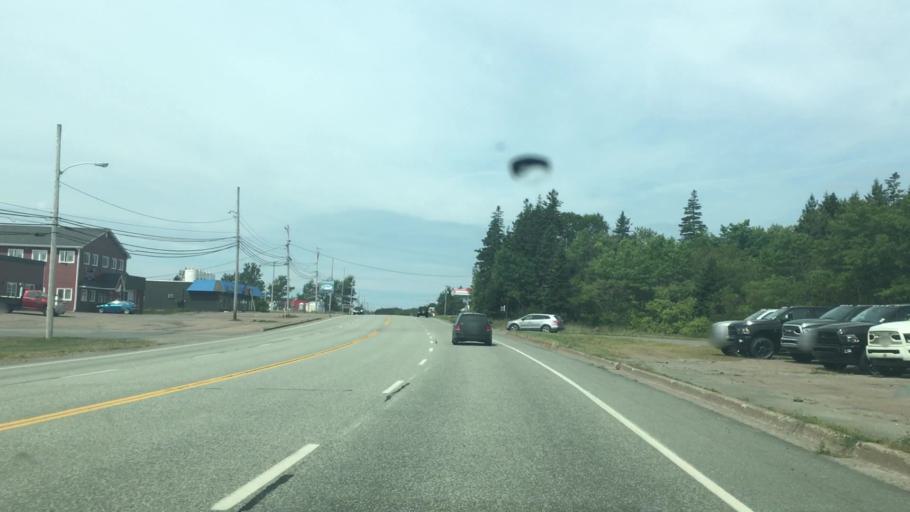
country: CA
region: Nova Scotia
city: Port Hawkesbury
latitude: 45.6395
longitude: -61.3852
